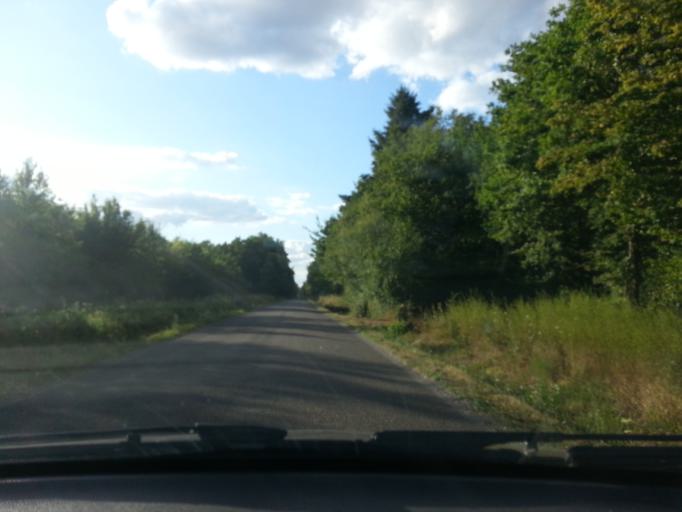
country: FR
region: Bourgogne
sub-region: Departement de Saone-et-Loire
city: Dracy-le-Fort
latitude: 46.7620
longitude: 4.7747
